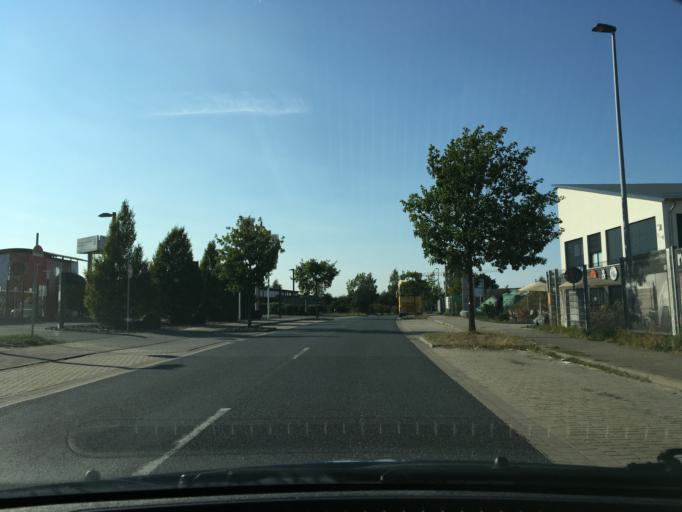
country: DE
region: Lower Saxony
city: Isernhagen Farster Bauerschaft
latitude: 52.4855
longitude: 9.8460
